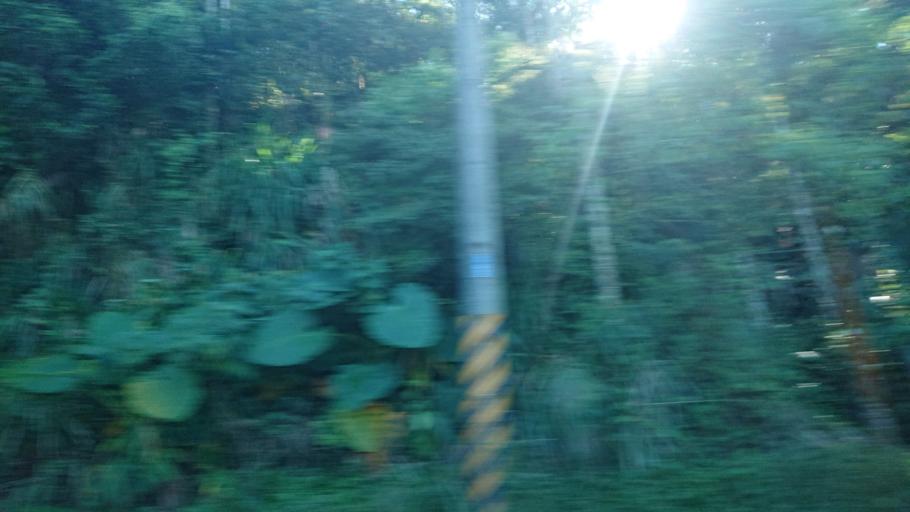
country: TW
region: Taiwan
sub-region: Chiayi
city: Jiayi Shi
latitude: 23.5227
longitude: 120.6321
